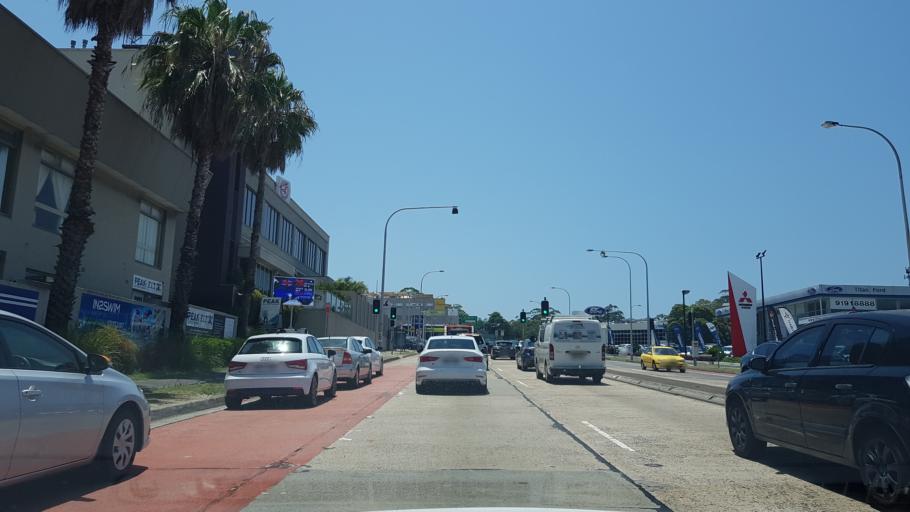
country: AU
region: New South Wales
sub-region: Warringah
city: Brookvale
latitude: -33.7606
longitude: 151.2777
